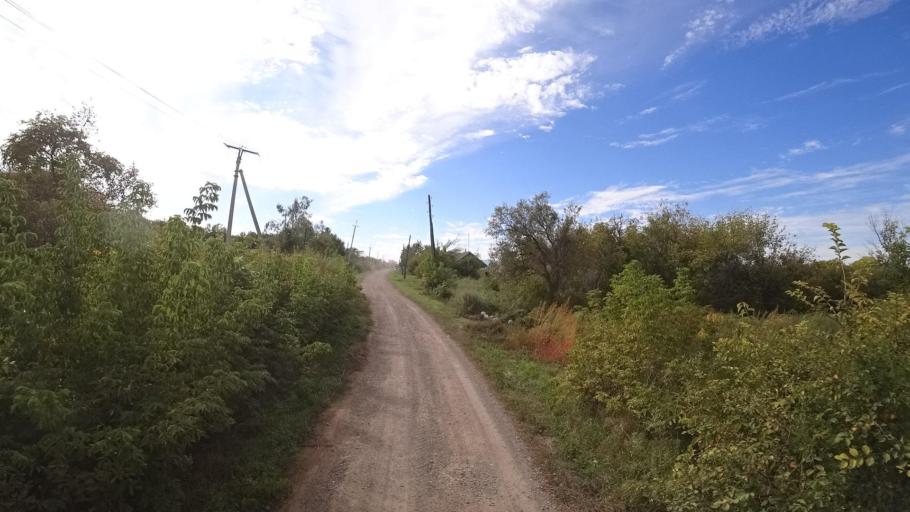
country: RU
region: Primorskiy
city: Dostoyevka
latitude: 44.3284
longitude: 133.4847
